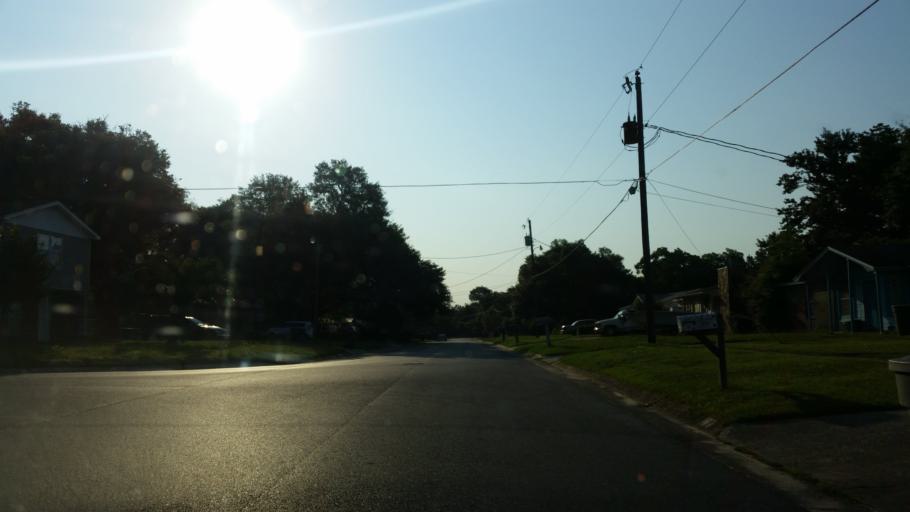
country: US
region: Florida
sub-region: Escambia County
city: Bellview
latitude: 30.4463
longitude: -87.3083
